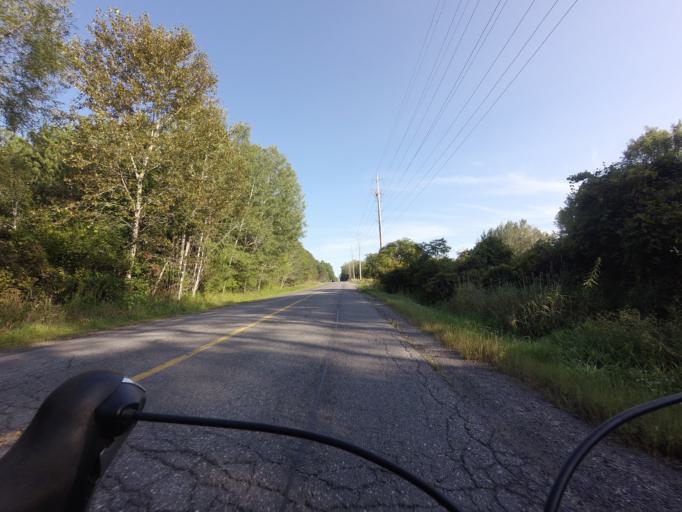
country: CA
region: Ontario
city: Bells Corners
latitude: 45.4609
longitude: -76.0218
